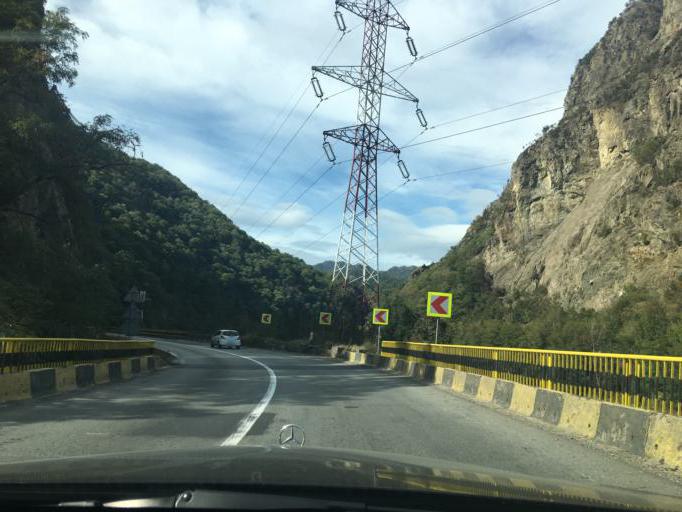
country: RO
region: Valcea
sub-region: Comuna Brezoi
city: Brezoi
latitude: 45.2925
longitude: 24.2948
